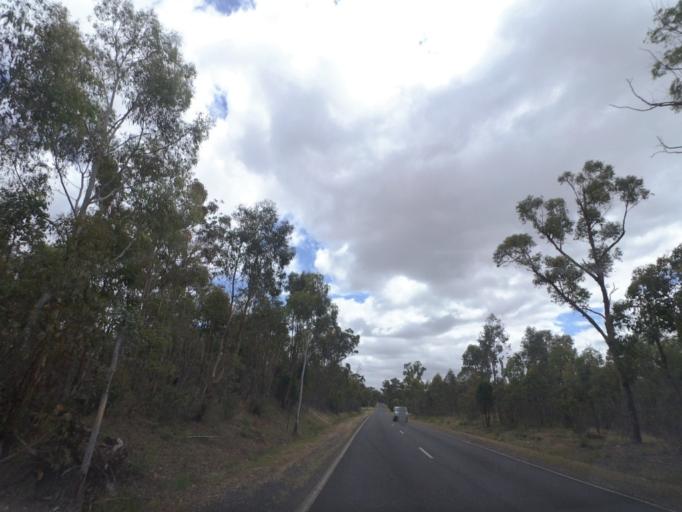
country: AU
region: Victoria
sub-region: Whittlesea
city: Whittlesea
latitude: -37.2944
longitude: 145.0574
